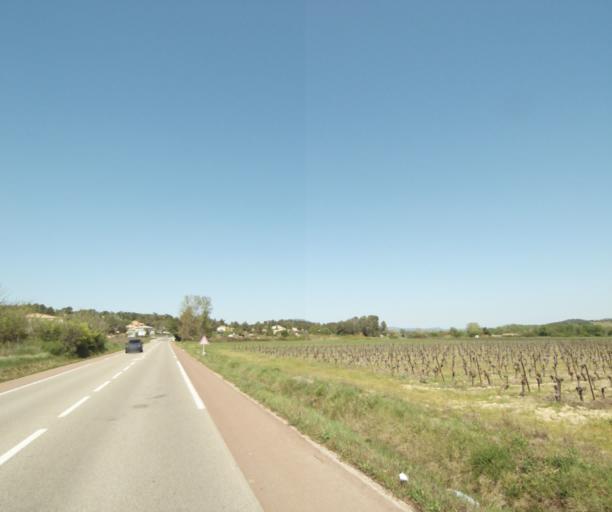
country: FR
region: Languedoc-Roussillon
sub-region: Departement de l'Herault
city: Montferrier-sur-Lez
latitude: 43.6753
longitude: 3.8579
